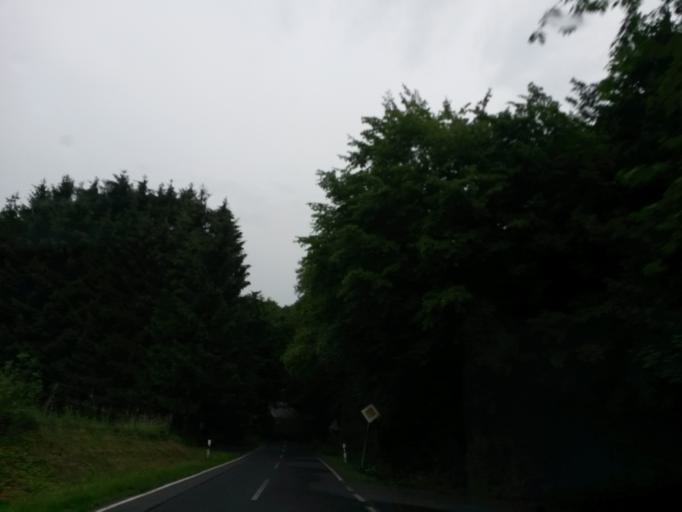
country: DE
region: North Rhine-Westphalia
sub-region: Regierungsbezirk Koln
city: Engelskirchen
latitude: 50.9526
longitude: 7.3644
